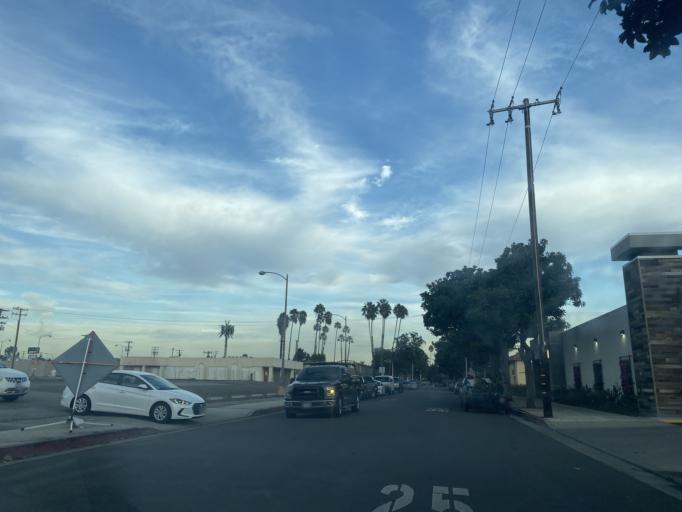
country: US
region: California
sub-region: Orange County
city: Fullerton
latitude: 33.8725
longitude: -117.9065
